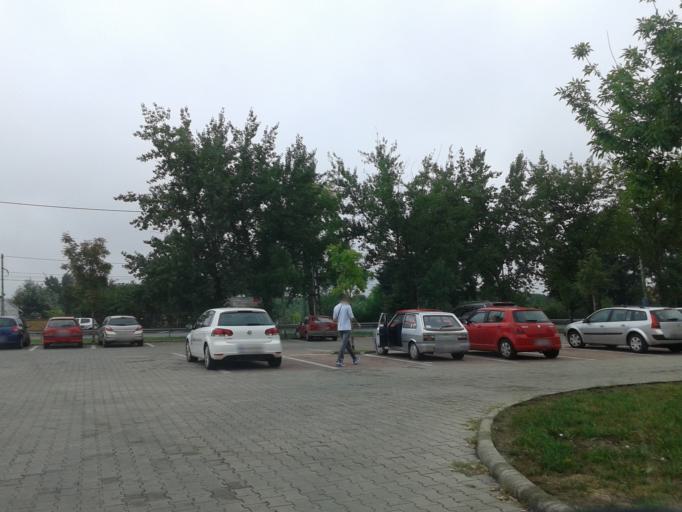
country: HU
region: Csongrad
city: Szeged
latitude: 46.2427
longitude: 20.1260
